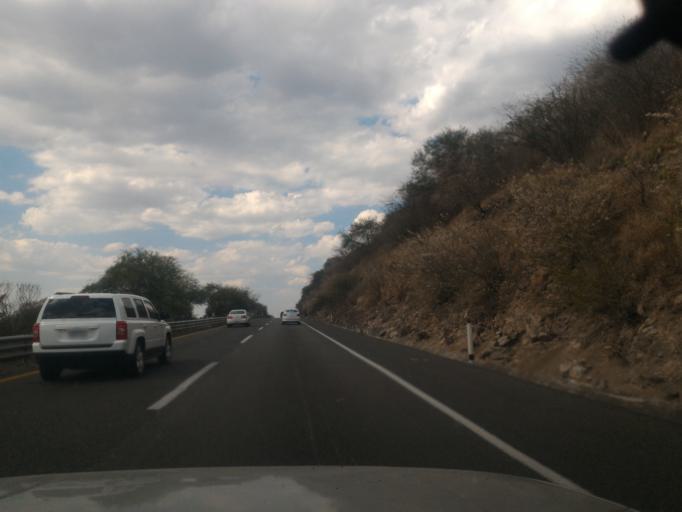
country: MX
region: Jalisco
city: Zacoalco de Torres
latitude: 20.1950
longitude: -103.5229
